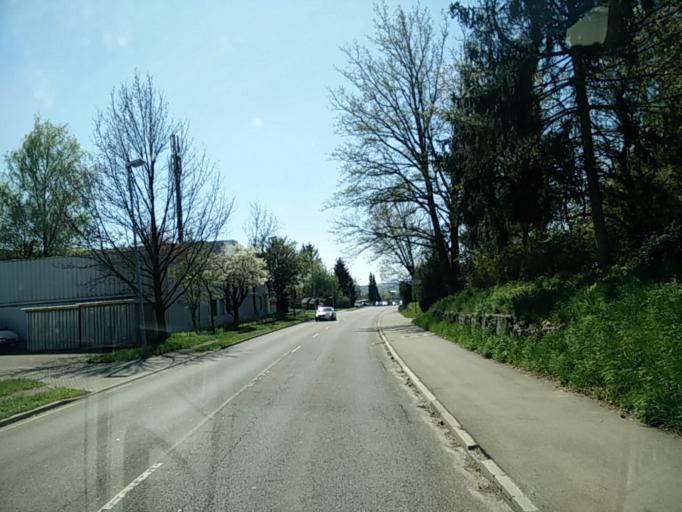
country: DE
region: Baden-Wuerttemberg
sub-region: Tuebingen Region
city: Gomaringen
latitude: 48.4551
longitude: 9.0950
